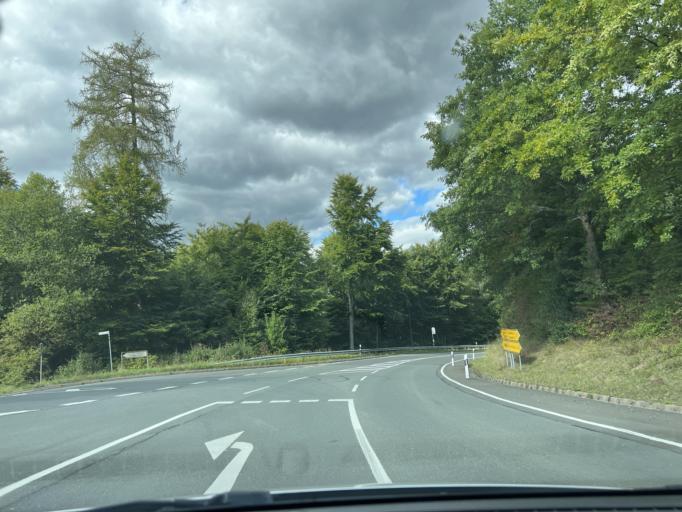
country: DE
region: North Rhine-Westphalia
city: Hilchenbach
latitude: 50.9801
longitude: 8.1449
